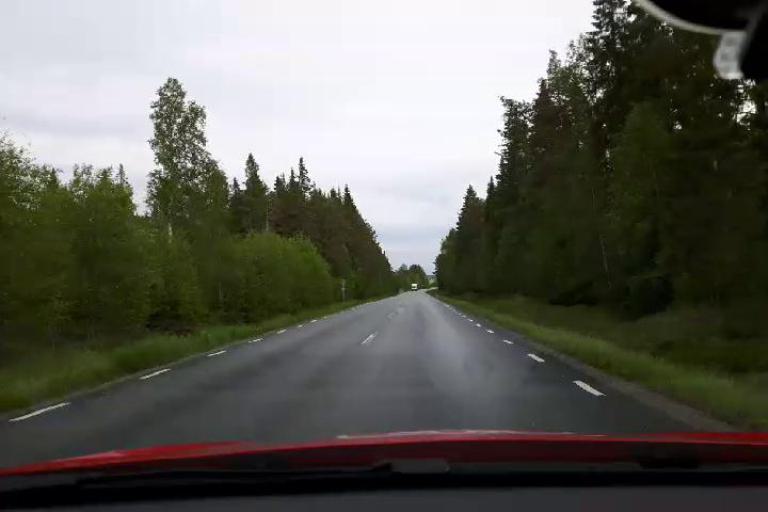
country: SE
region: Jaemtland
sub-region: Bergs Kommun
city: Hoverberg
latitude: 62.9840
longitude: 14.4445
